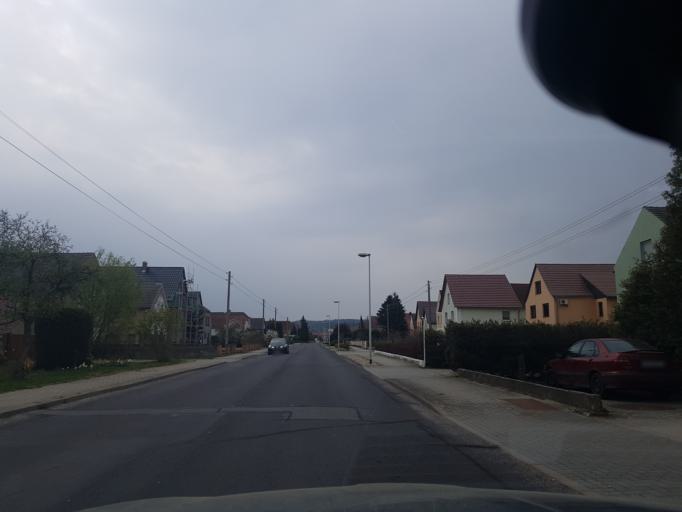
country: DE
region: Brandenburg
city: Grosskmehlen
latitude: 51.3882
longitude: 13.7107
